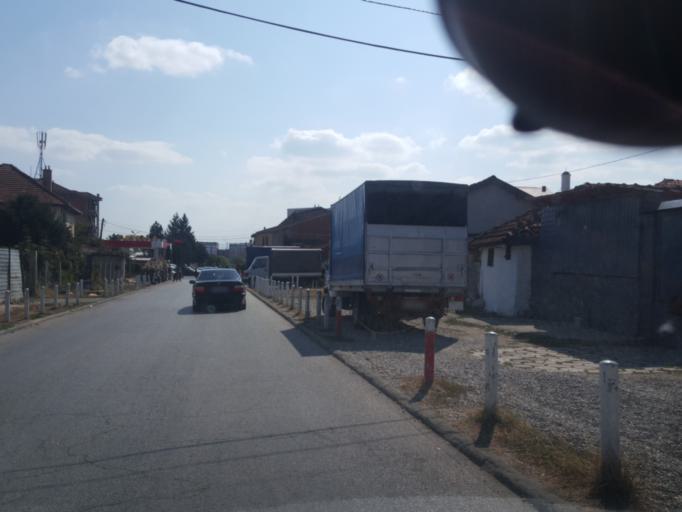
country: XK
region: Gjakova
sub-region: Komuna e Gjakoves
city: Gjakove
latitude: 42.3894
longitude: 20.4306
